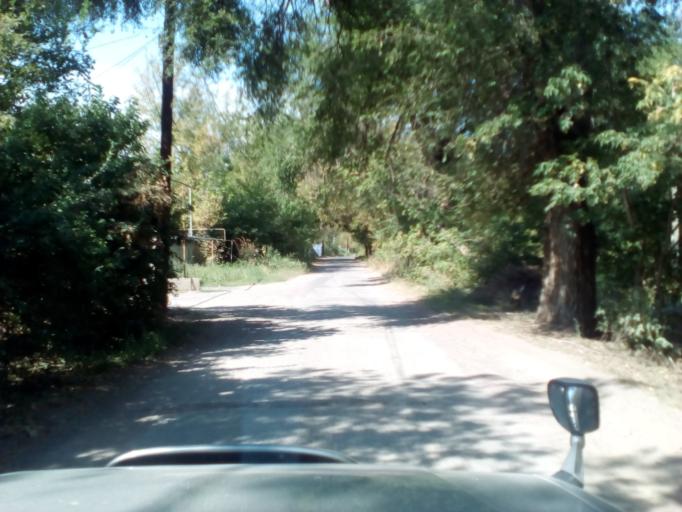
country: KZ
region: Almaty Oblysy
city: Burunday
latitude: 43.1595
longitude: 76.3916
